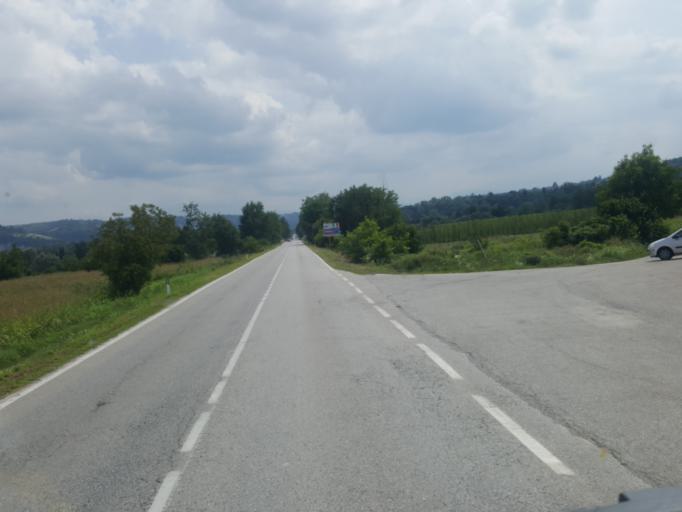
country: IT
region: Piedmont
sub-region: Provincia di Cuneo
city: Piozzo
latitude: 44.5206
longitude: 7.9005
